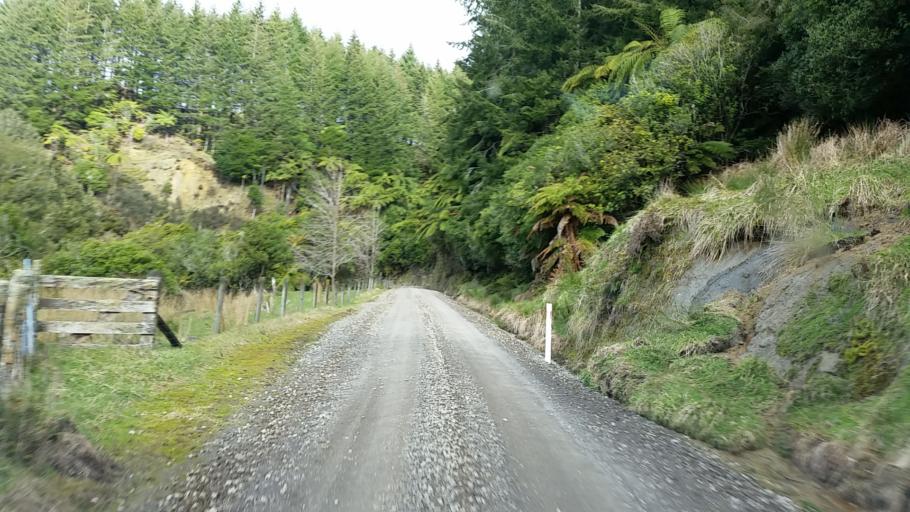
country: NZ
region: Taranaki
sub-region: South Taranaki District
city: Eltham
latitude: -39.1726
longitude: 174.6147
